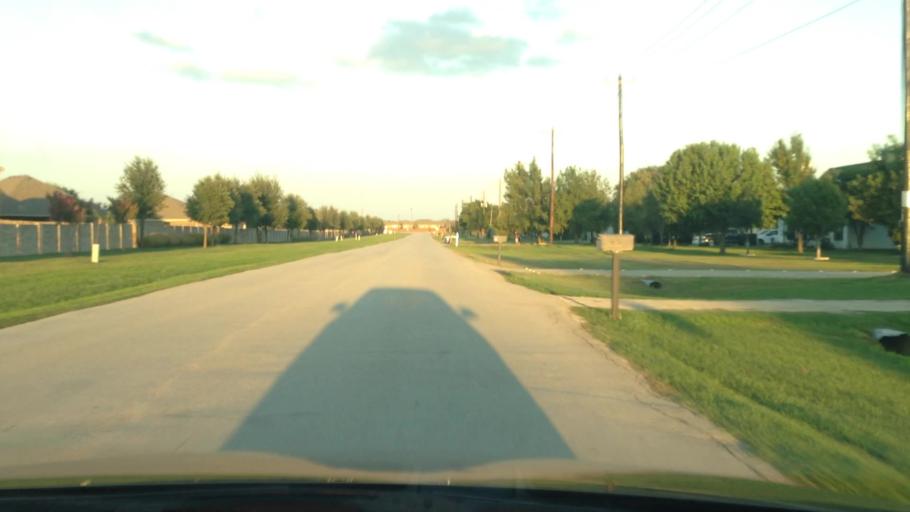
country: US
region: Texas
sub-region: Denton County
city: Little Elm
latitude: 33.1361
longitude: -96.9276
